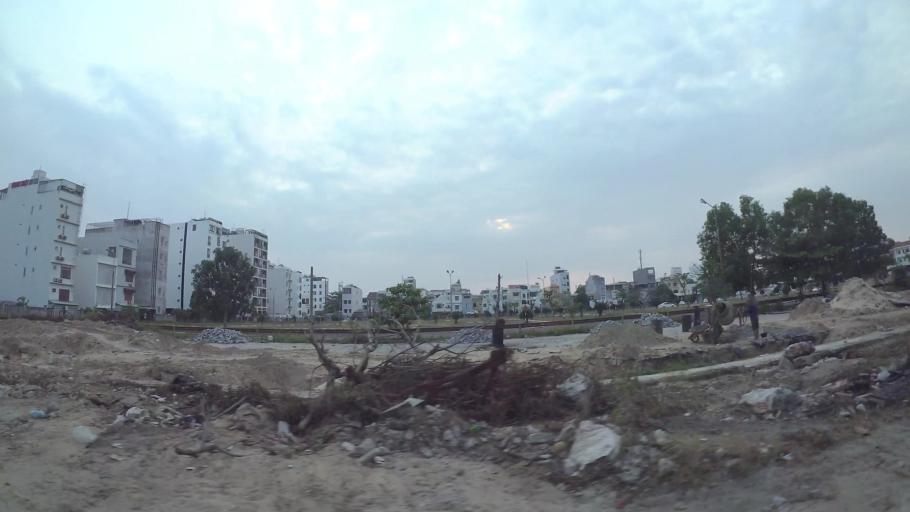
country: VN
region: Da Nang
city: Son Tra
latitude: 16.0495
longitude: 108.2430
